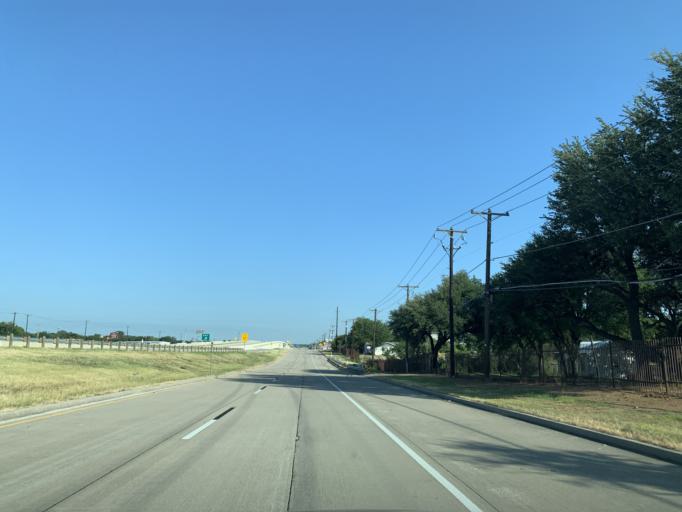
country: US
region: Texas
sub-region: Tarrant County
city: Lakeside
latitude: 32.8340
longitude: -97.4869
